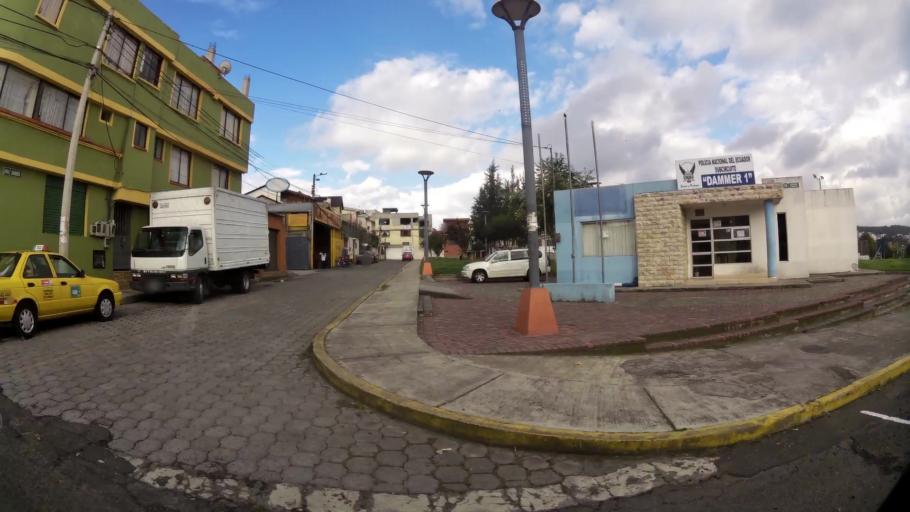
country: EC
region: Pichincha
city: Quito
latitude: -0.1487
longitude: -78.4743
